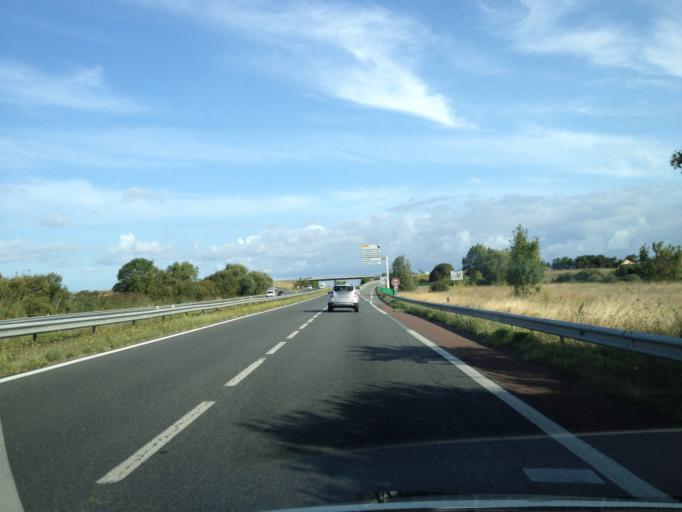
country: FR
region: Poitou-Charentes
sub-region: Departement de la Charente-Maritime
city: Chatelaillon-Plage
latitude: 46.0599
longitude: -1.0595
